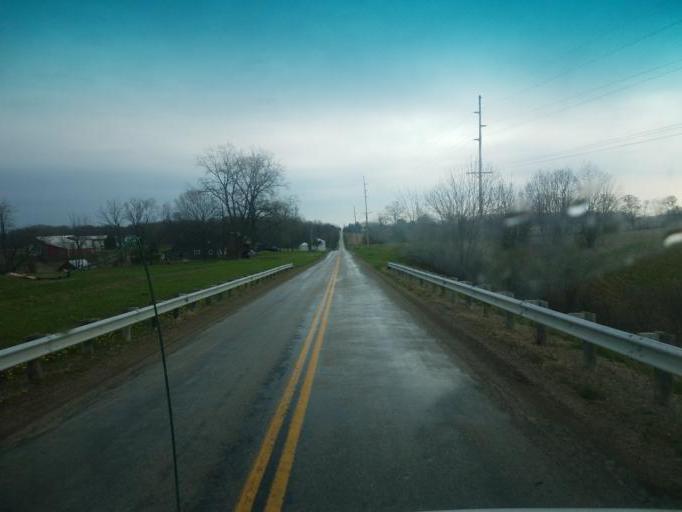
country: US
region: Ohio
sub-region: Ashland County
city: Ashland
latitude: 40.8288
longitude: -82.3169
